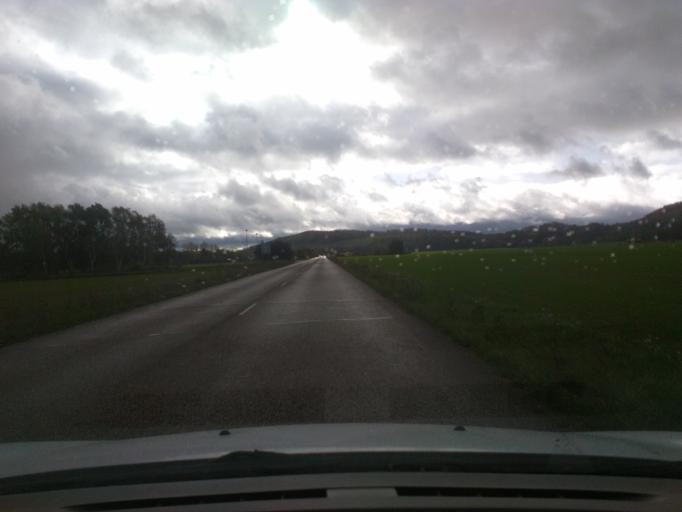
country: FR
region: Lorraine
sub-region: Departement des Vosges
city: Charmes
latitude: 48.3863
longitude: 6.2629
